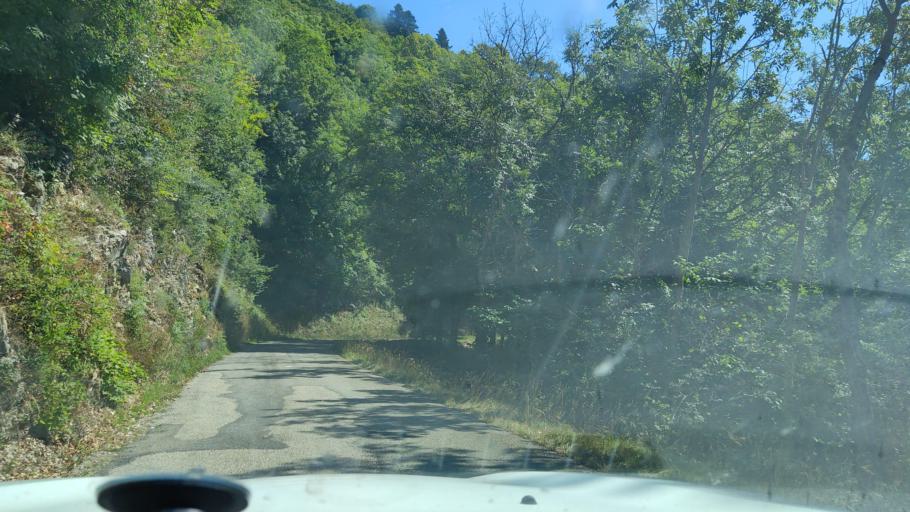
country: FR
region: Rhone-Alpes
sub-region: Departement de la Savoie
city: Le Bourget-du-Lac
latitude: 45.6458
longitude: 5.8089
